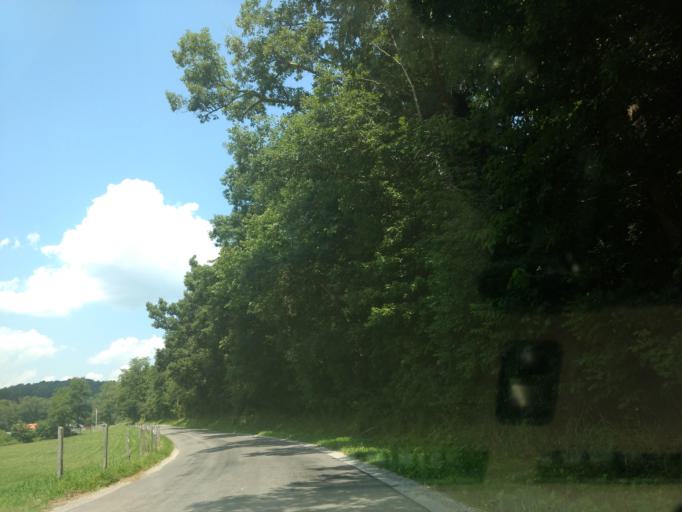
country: US
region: Pennsylvania
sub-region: Butler County
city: Evans City
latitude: 40.8341
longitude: -80.0742
